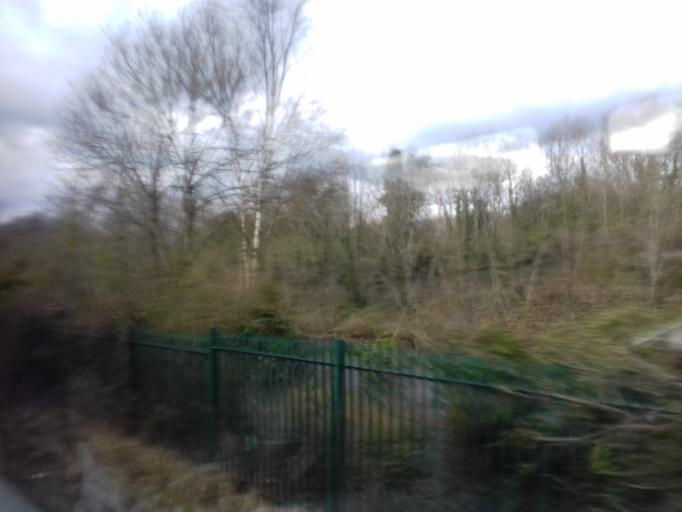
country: IE
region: Leinster
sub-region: An Iarmhi
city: An Muileann gCearr
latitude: 53.5162
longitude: -7.3277
